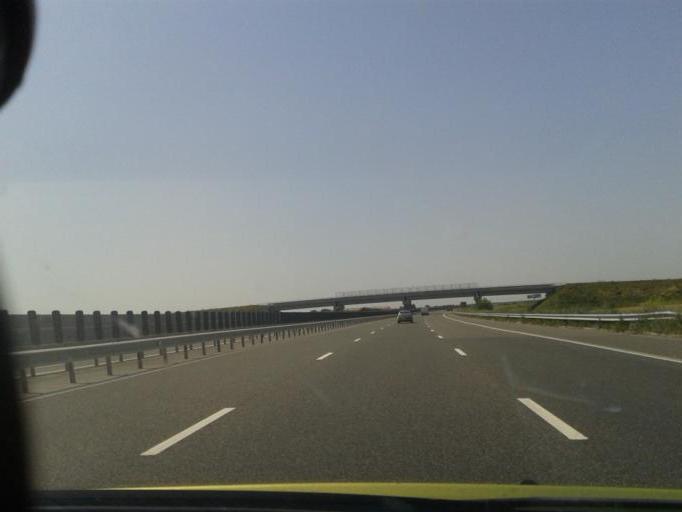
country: RO
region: Ilfov
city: Stefanestii de Jos
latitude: 44.5438
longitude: 26.1846
